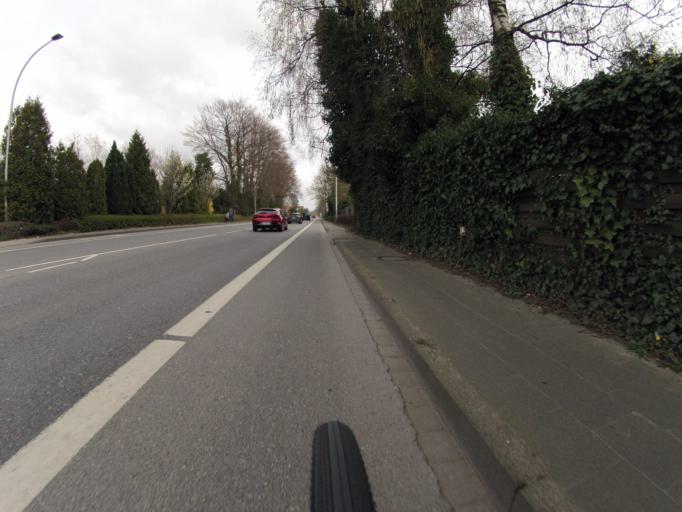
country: DE
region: North Rhine-Westphalia
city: Ibbenburen
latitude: 52.2913
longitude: 7.7149
